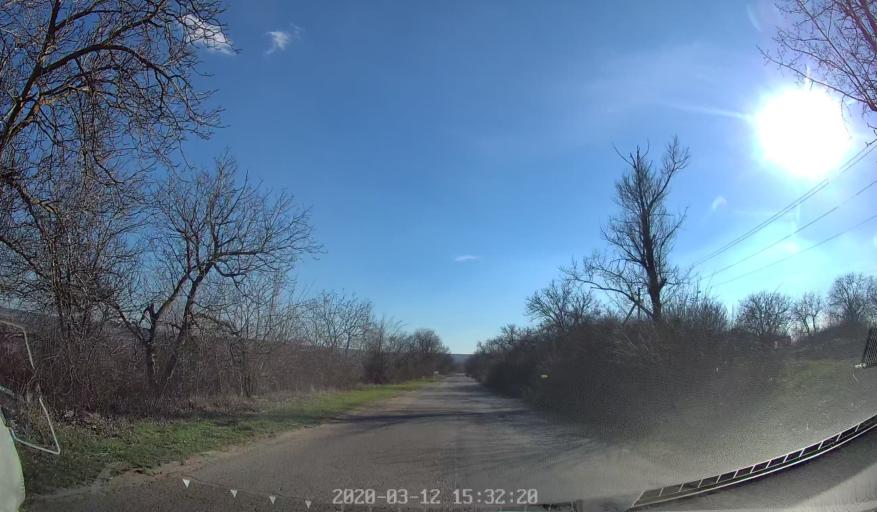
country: MD
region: Chisinau
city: Ciorescu
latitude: 47.1526
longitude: 28.9412
